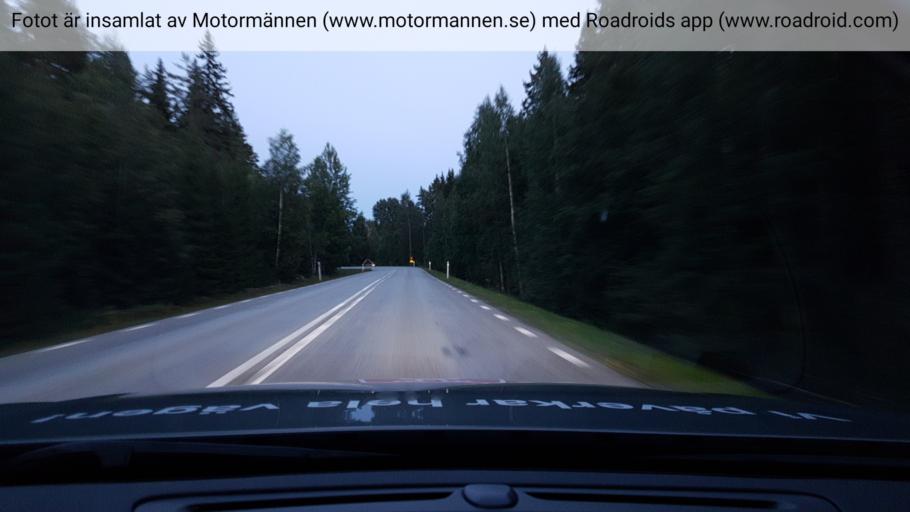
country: SE
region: OErebro
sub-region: Ljusnarsbergs Kommun
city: Kopparberg
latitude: 59.8705
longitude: 15.0428
